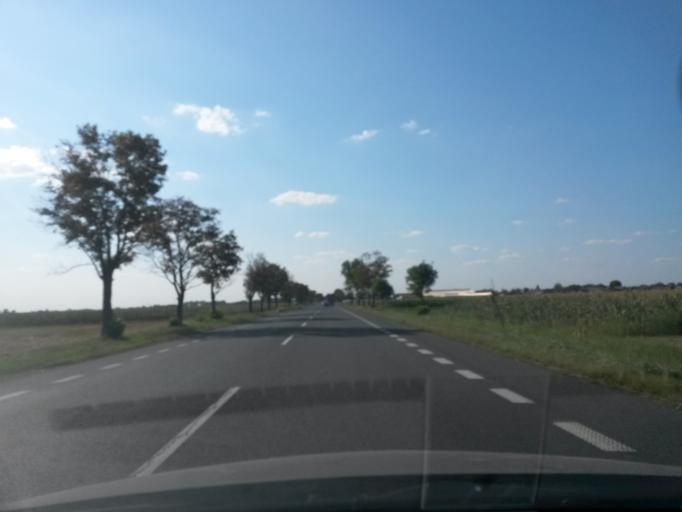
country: PL
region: Masovian Voivodeship
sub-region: Powiat sierpecki
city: Zawidz
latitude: 52.8026
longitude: 19.8506
